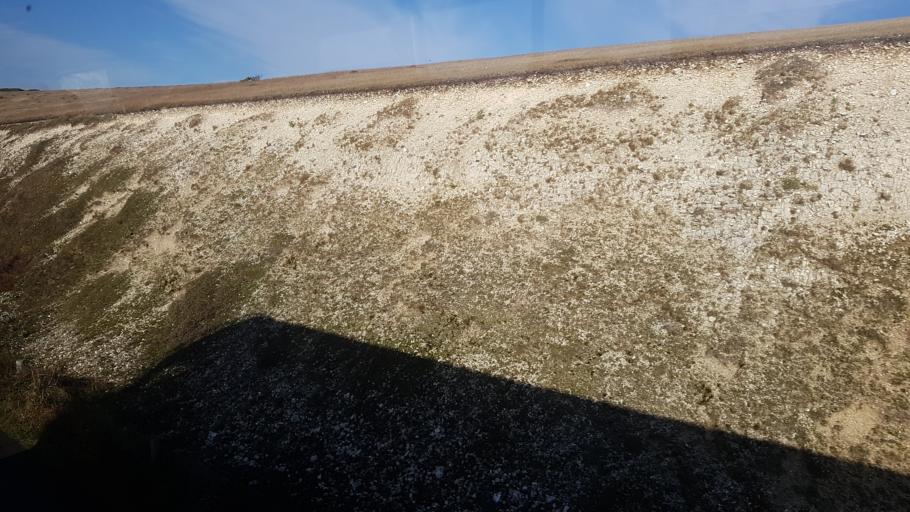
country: GB
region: England
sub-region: Isle of Wight
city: Freshwater
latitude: 50.6690
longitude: -1.4915
